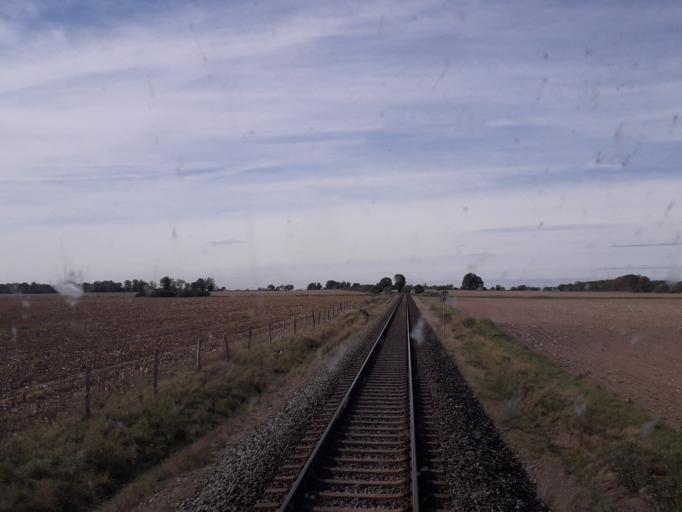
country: DE
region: Brandenburg
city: Ruthnick
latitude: 52.8609
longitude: 12.8901
